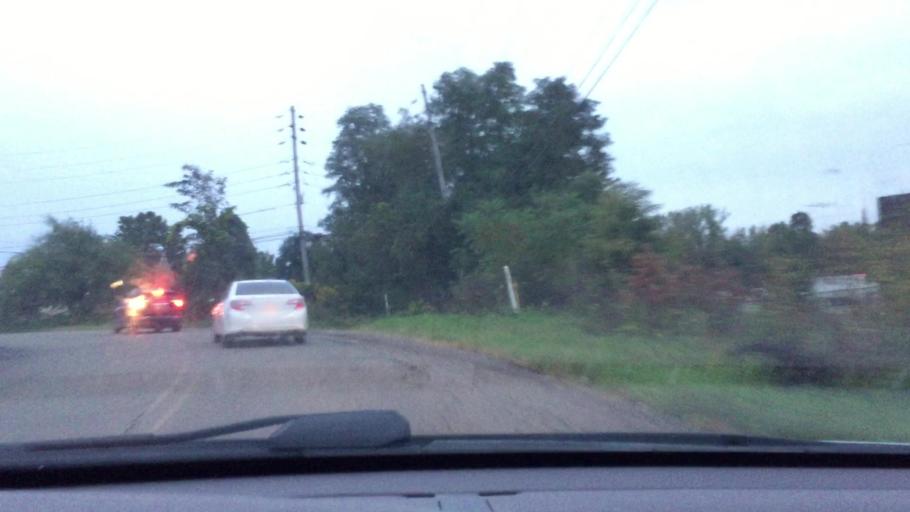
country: US
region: Pennsylvania
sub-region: Allegheny County
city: Cheswick
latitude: 40.5569
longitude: -79.8235
